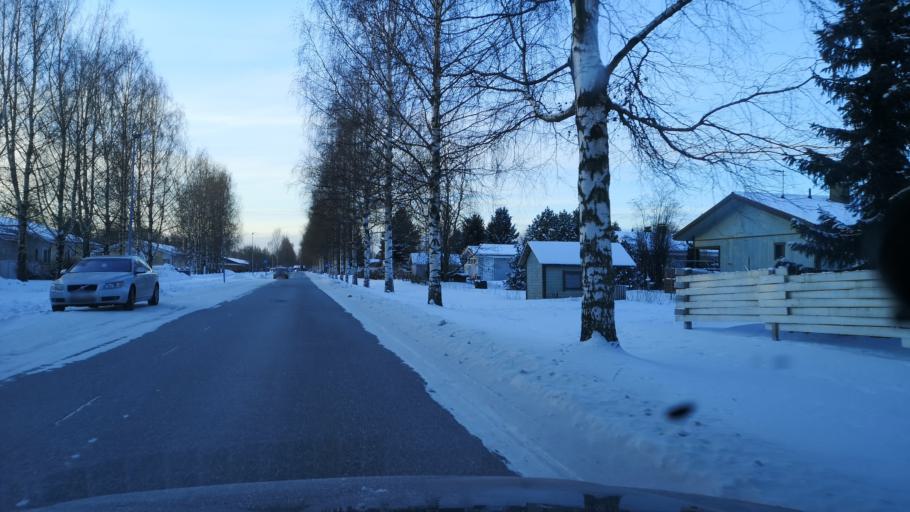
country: FI
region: Satakunta
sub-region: Pori
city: Pori
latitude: 61.5038
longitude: 21.8244
